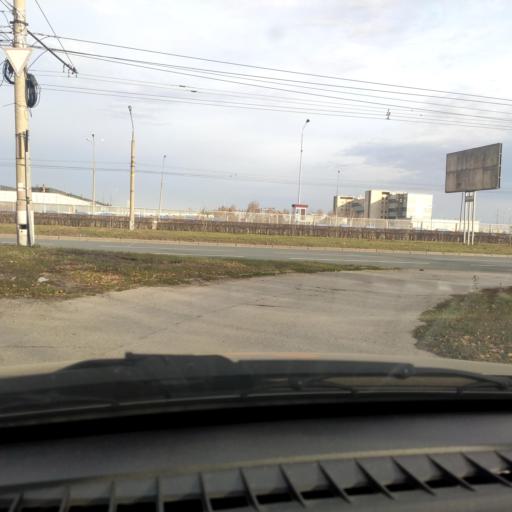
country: RU
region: Samara
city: Tol'yatti
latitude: 53.5536
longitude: 49.2805
